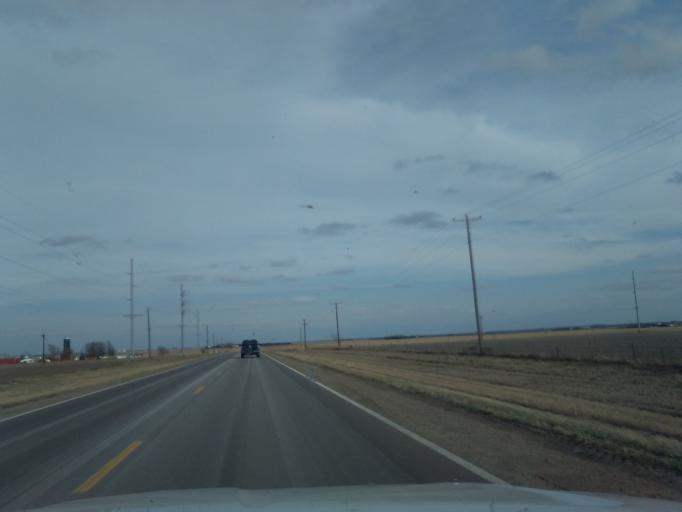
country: US
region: Nebraska
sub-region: Saline County
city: Wilber
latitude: 40.3062
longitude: -96.9381
